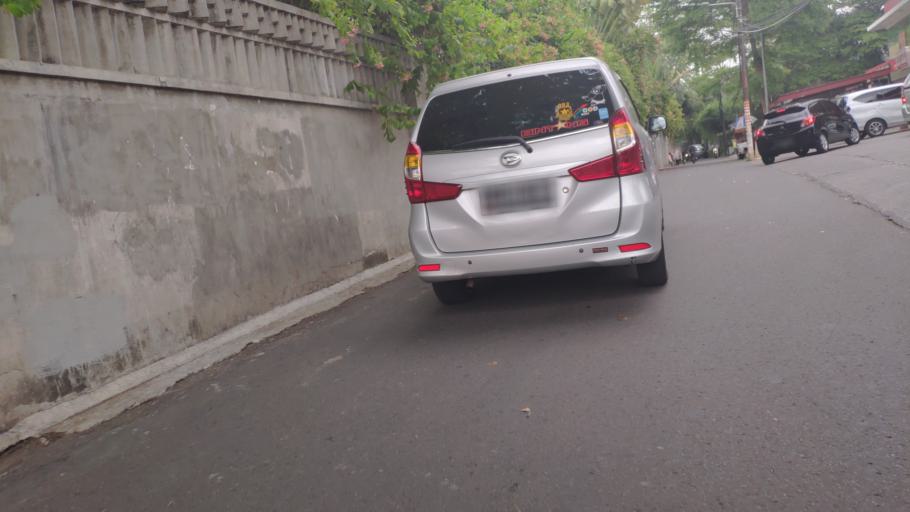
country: ID
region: Jakarta Raya
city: Jakarta
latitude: -6.2736
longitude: 106.8186
